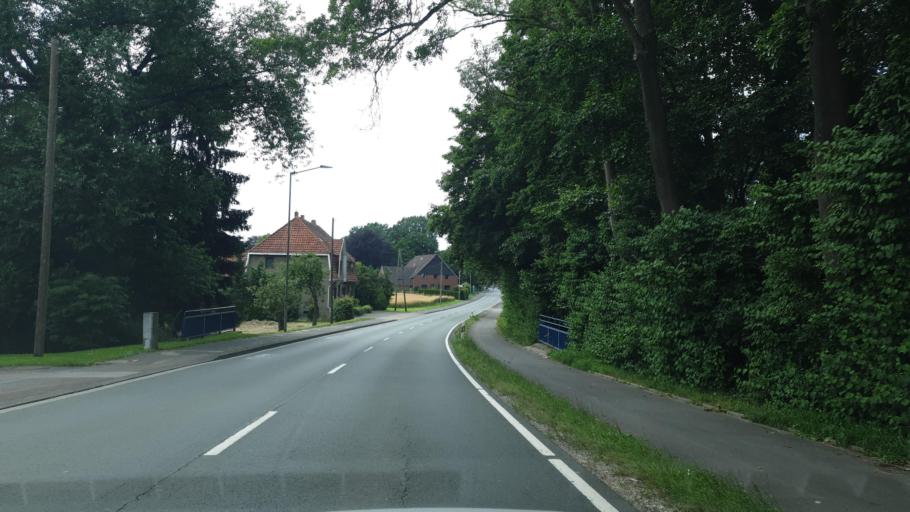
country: DE
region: North Rhine-Westphalia
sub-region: Regierungsbezirk Detmold
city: Bad Salzuflen
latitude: 52.1351
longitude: 8.7846
